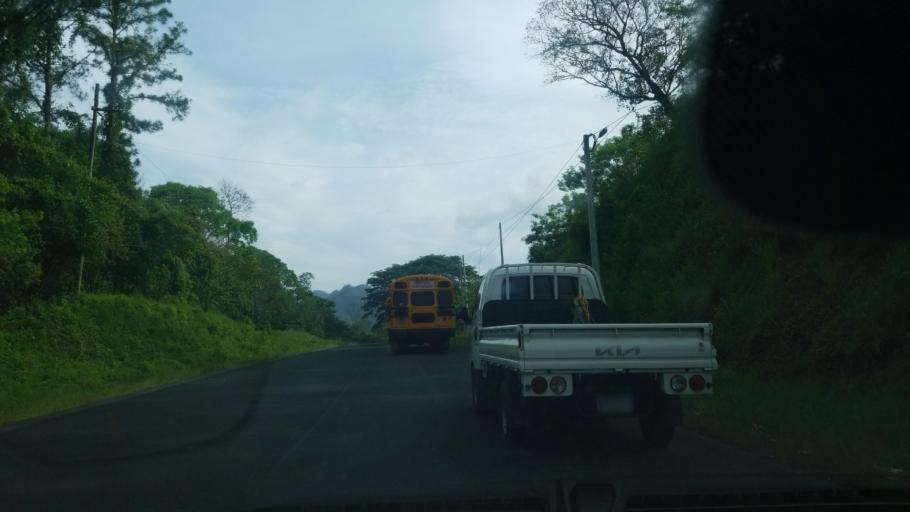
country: HN
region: Santa Barbara
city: Petoa
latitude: 15.2088
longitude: -88.2687
